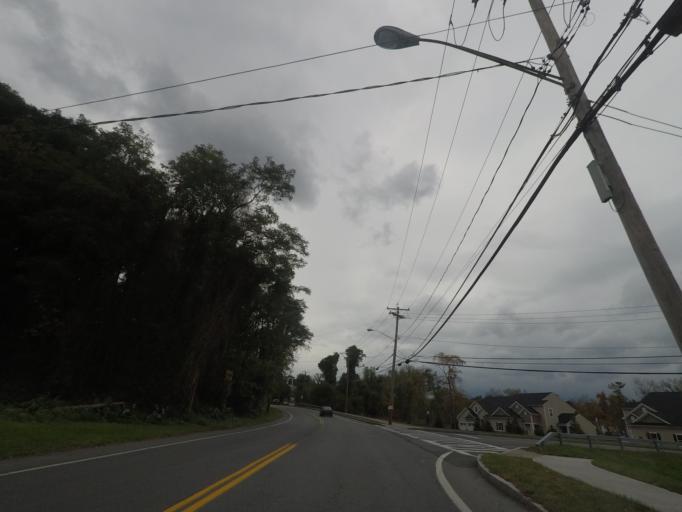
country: US
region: New York
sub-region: Albany County
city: McKownville
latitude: 42.6634
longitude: -73.8437
